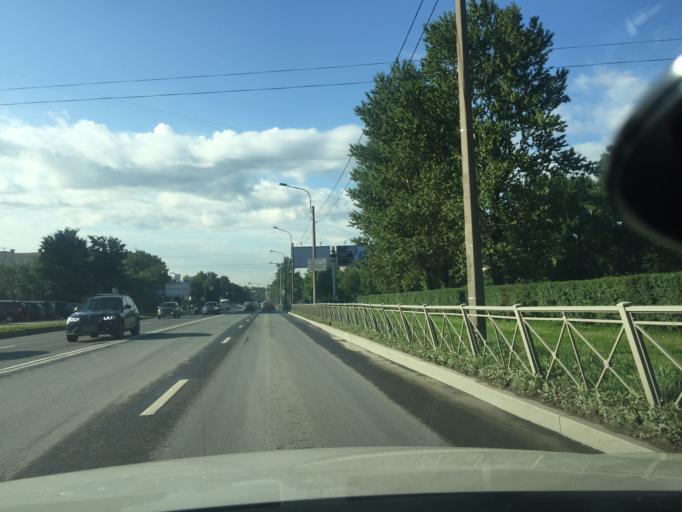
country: RU
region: St.-Petersburg
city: Kupchino
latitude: 59.8463
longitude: 30.3378
